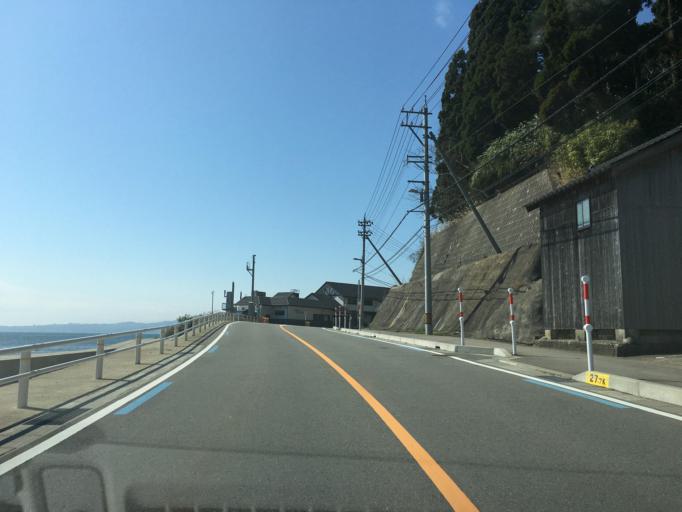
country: JP
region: Toyama
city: Himi
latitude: 36.9007
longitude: 137.0114
